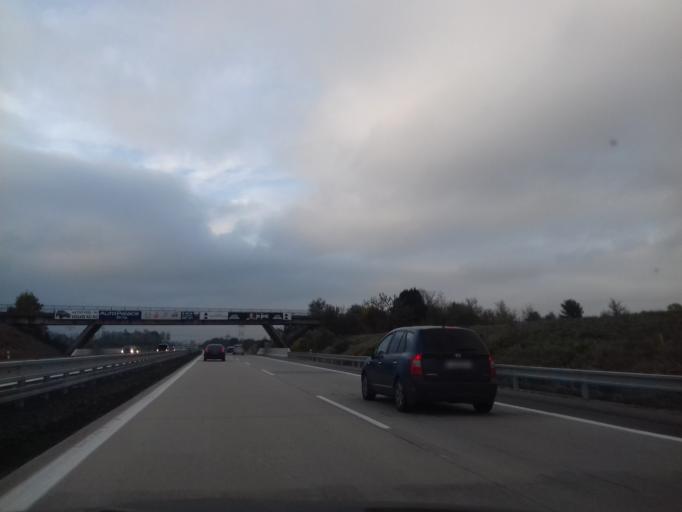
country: CZ
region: South Moravian
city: Rajhradice
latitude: 49.1131
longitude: 16.6498
